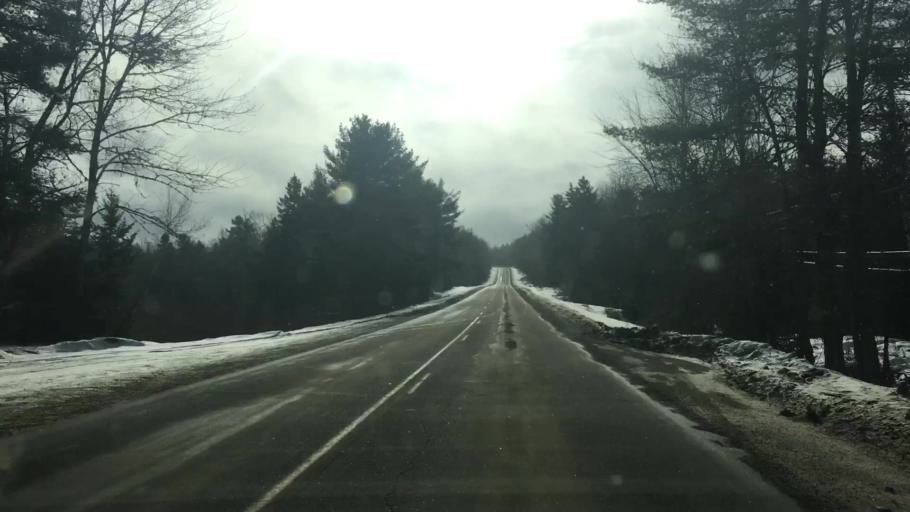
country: US
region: Maine
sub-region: Washington County
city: Calais
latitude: 45.0734
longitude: -67.3320
